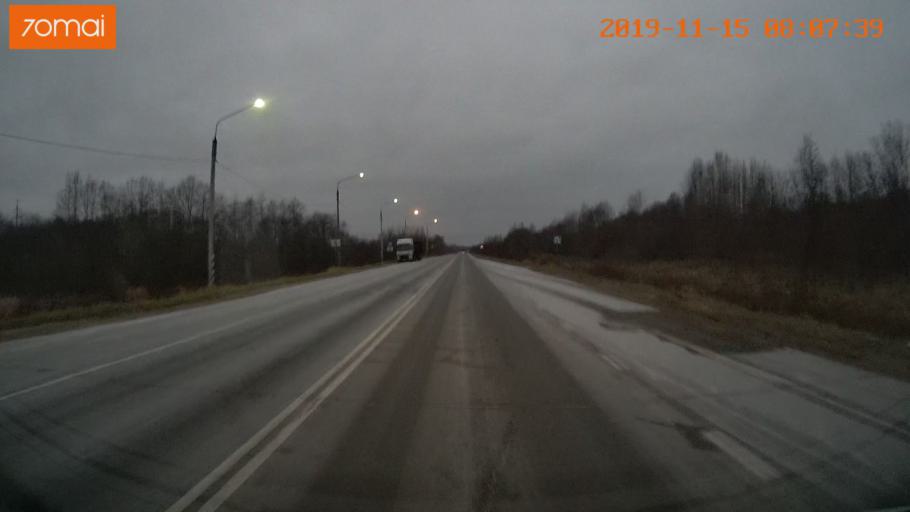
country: RU
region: Vologda
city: Cherepovets
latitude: 59.0269
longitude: 38.0140
